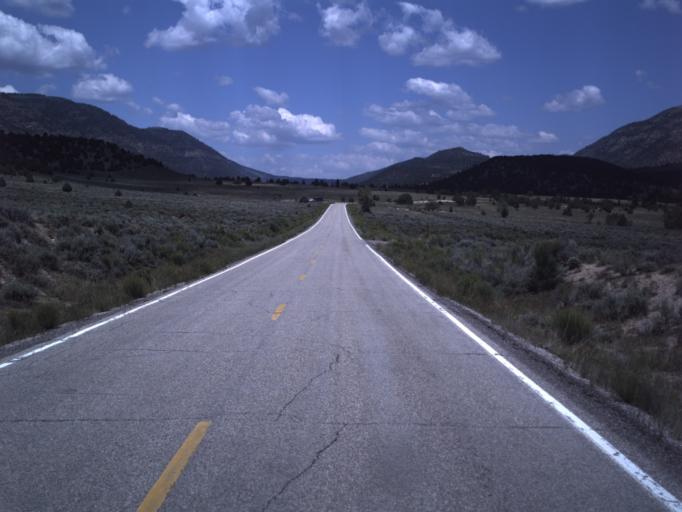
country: US
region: Utah
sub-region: Emery County
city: Orangeville
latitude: 39.3172
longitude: -111.2829
